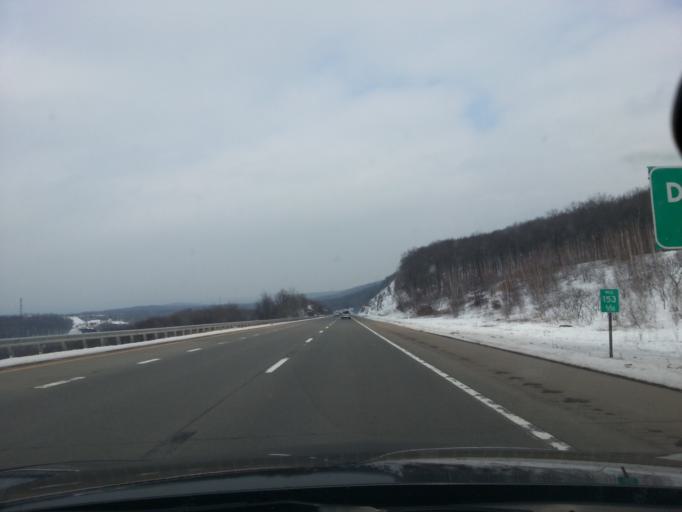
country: US
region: Pennsylvania
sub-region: Luzerne County
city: Harleigh
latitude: 41.0731
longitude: -75.9787
